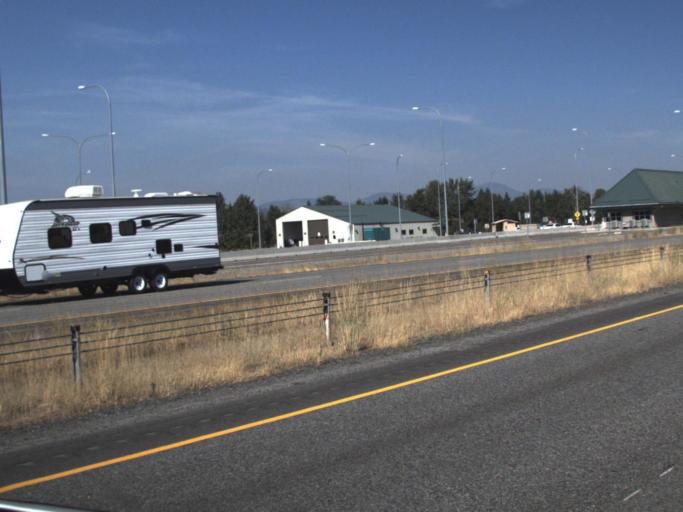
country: US
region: Washington
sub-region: Spokane County
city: Otis Orchards-East Farms
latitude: 47.6869
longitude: -117.0721
